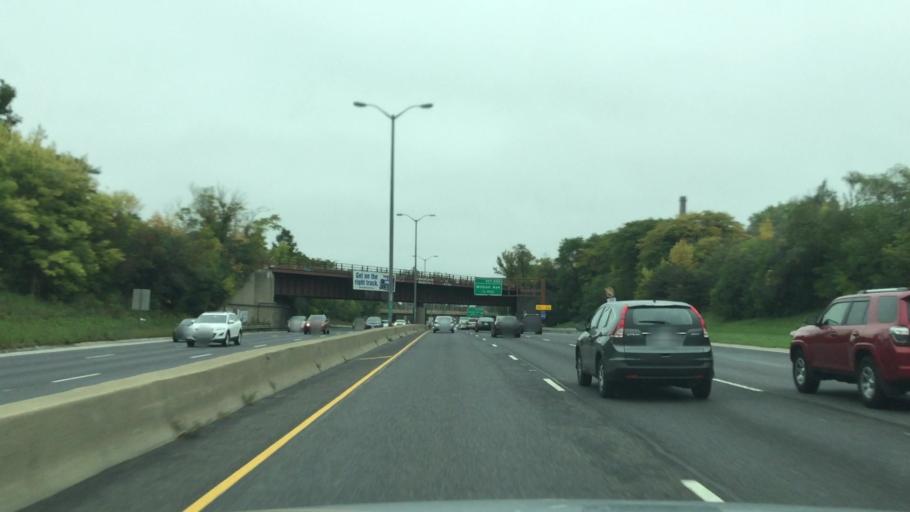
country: US
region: Illinois
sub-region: Cook County
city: Lincolnwood
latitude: 41.9709
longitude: -87.7474
